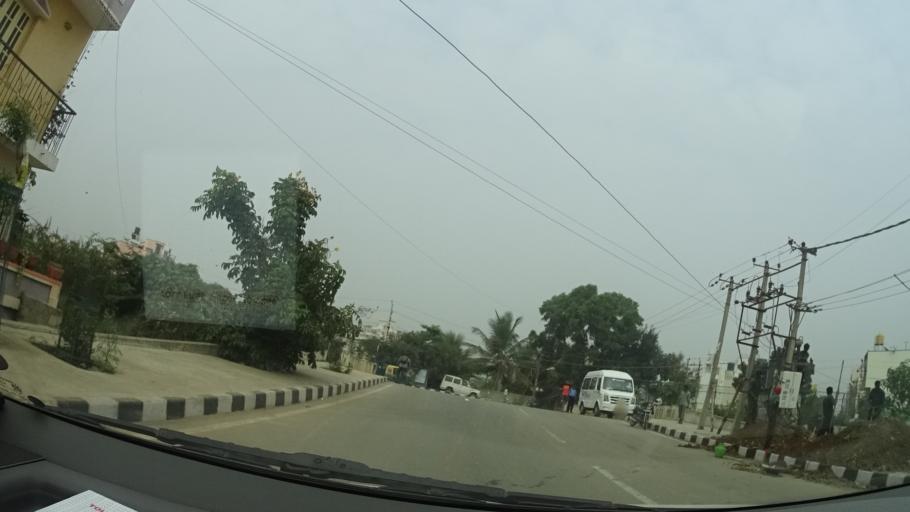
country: IN
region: Karnataka
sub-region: Bangalore Urban
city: Yelahanka
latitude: 13.0397
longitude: 77.6293
